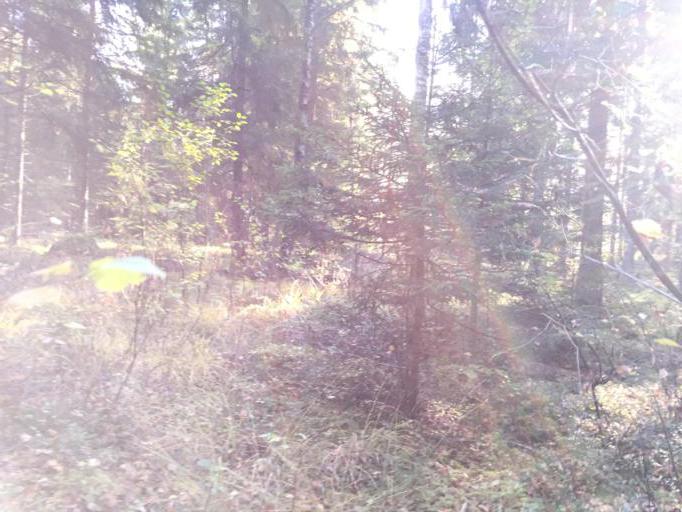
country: SE
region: Vaestra Goetaland
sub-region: Vara Kommun
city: Vara
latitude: 58.3775
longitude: 12.9335
